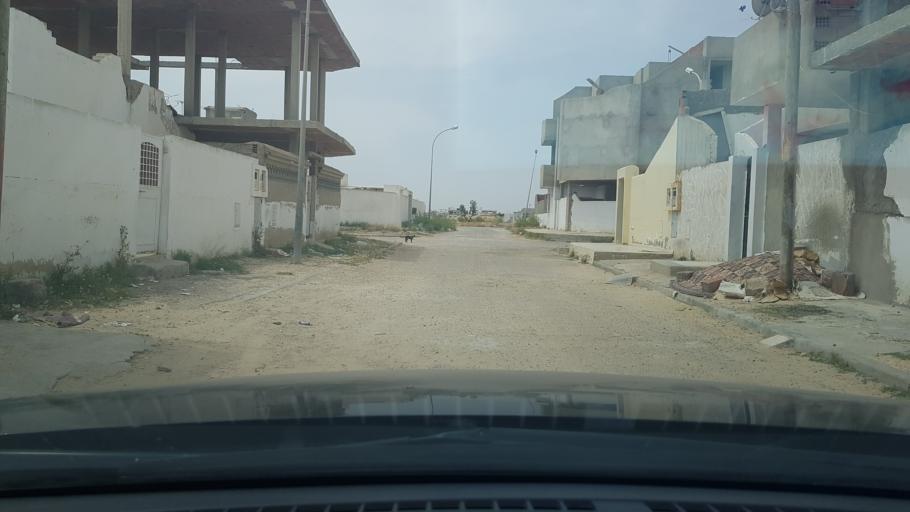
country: TN
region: Safaqis
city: Al Qarmadah
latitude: 34.8252
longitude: 10.7468
